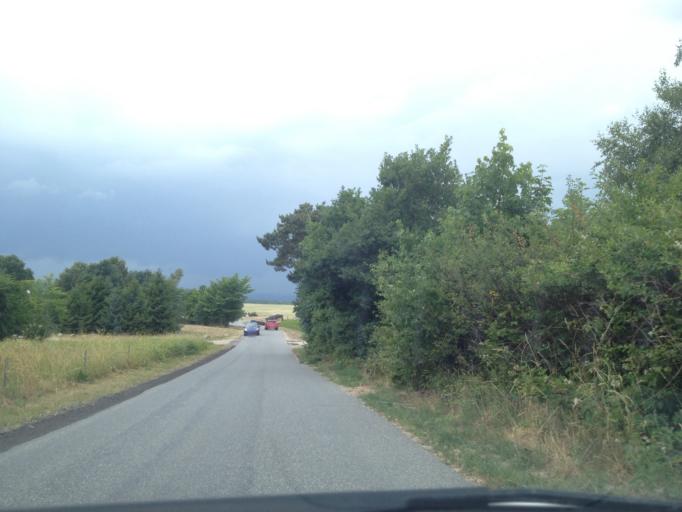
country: DK
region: Central Jutland
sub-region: Syddjurs Kommune
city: Ebeltoft
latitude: 56.1696
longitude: 10.6724
